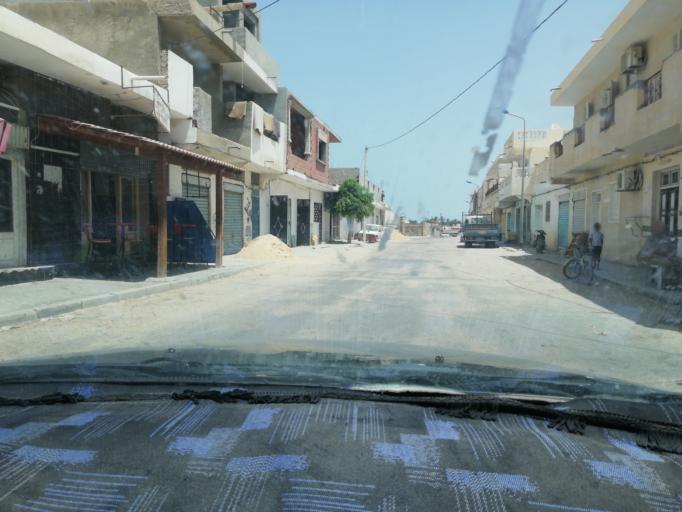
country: TN
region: Qabis
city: Gabes
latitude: 33.6213
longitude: 10.2808
